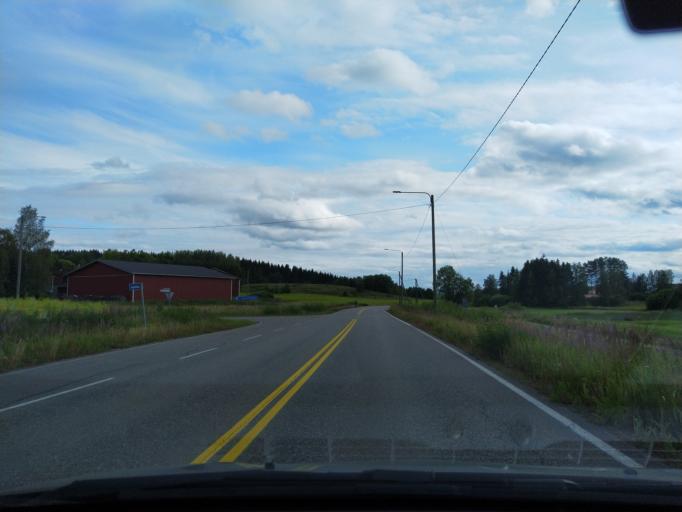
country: FI
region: Kymenlaakso
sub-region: Kouvola
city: Kouvola
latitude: 61.0454
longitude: 26.8298
